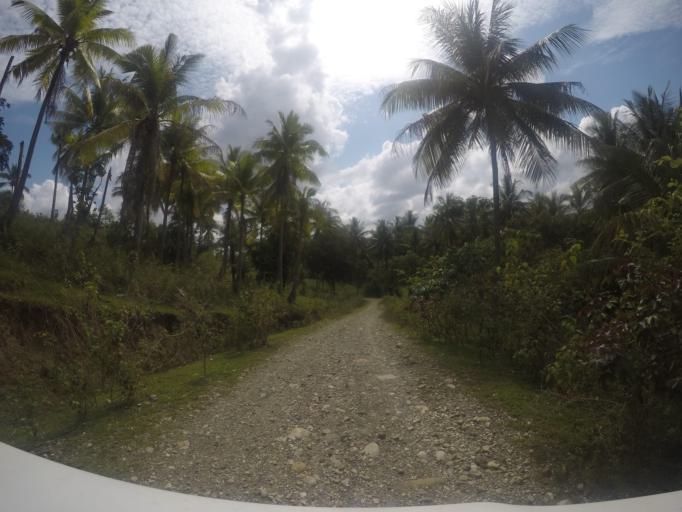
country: TL
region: Viqueque
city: Viqueque
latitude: -8.8498
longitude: 126.3610
